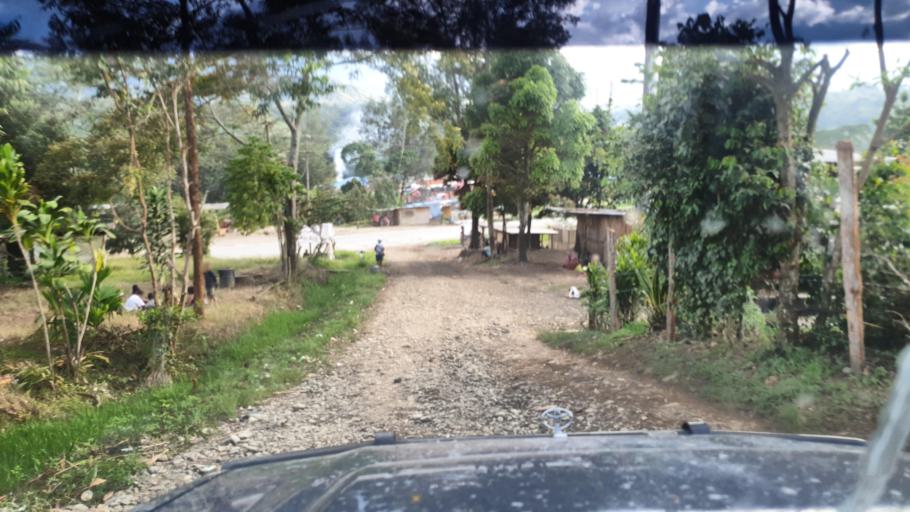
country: PG
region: Jiwaka
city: Minj
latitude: -5.9432
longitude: 144.8206
